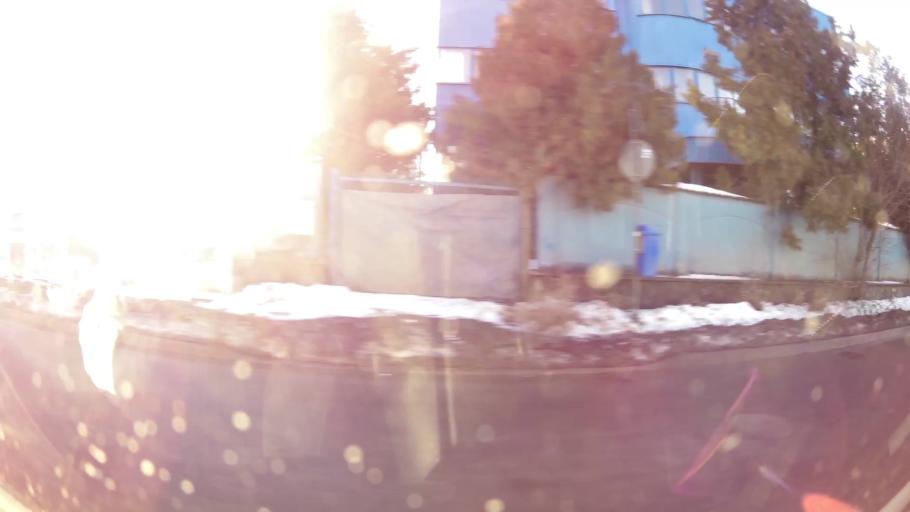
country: RO
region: Ilfov
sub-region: Comuna Fundeni-Dobroesti
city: Fundeni
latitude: 44.4747
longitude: 26.1407
